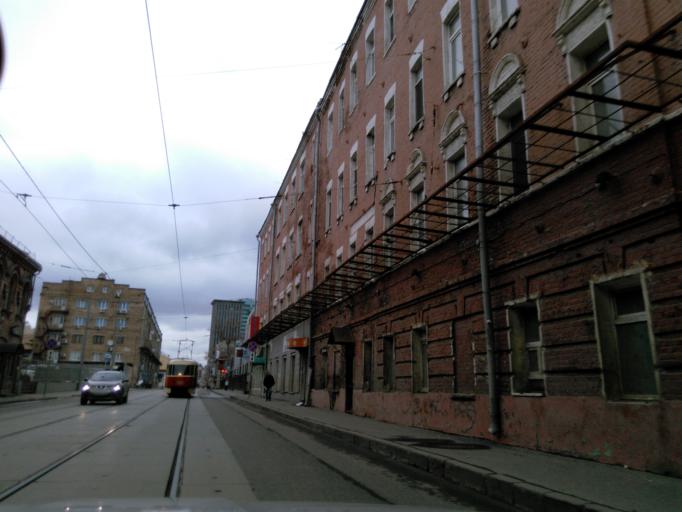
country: RU
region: Moscow
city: Zamoskvorech'ye
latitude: 55.7200
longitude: 37.6349
